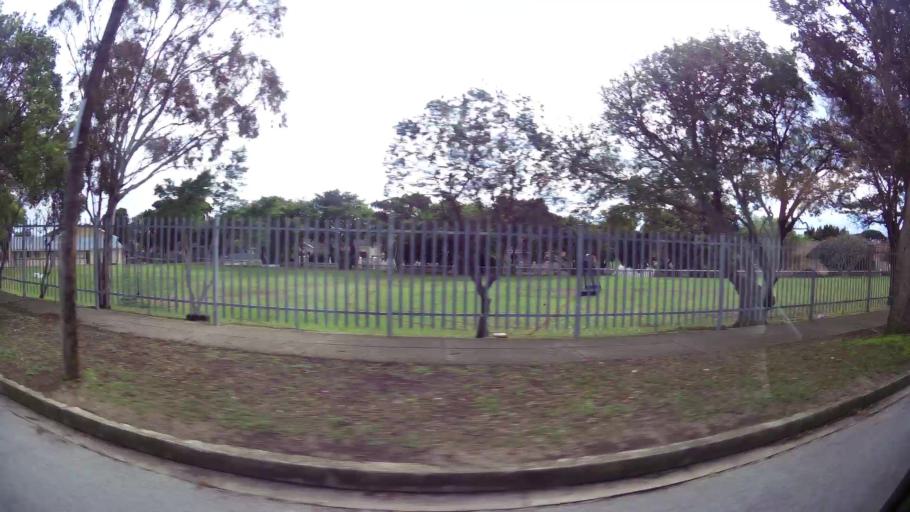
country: ZA
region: Eastern Cape
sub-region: Nelson Mandela Bay Metropolitan Municipality
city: Port Elizabeth
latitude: -33.9423
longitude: 25.5539
